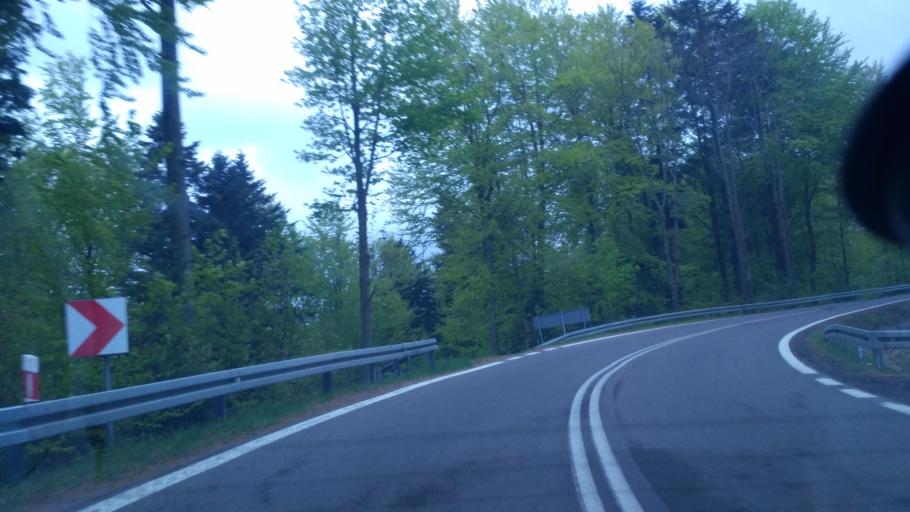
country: PL
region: Subcarpathian Voivodeship
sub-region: Powiat sanocki
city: Tyrawa Woloska
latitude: 49.5645
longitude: 22.3431
